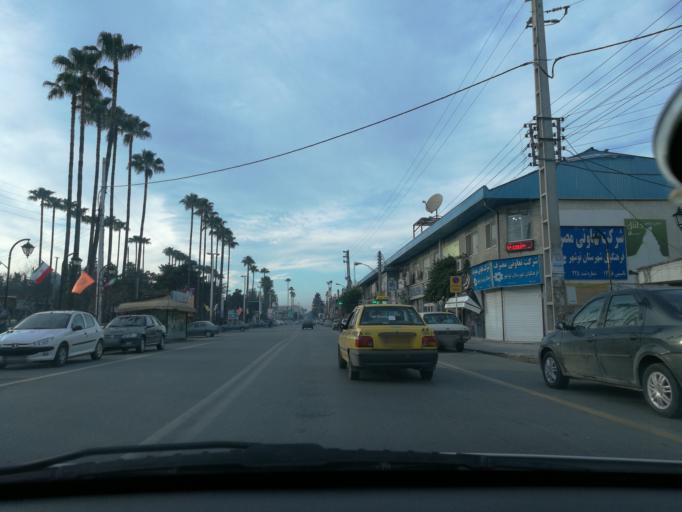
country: IR
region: Mazandaran
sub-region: Nowshahr
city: Nowshahr
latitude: 36.6513
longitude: 51.5044
